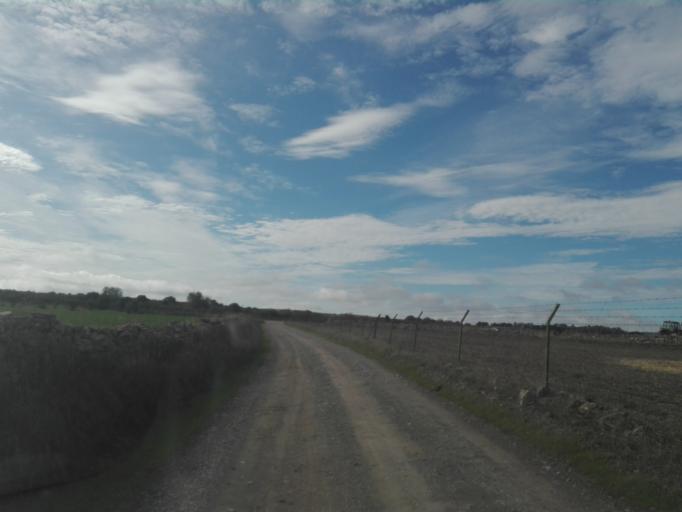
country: ES
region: Extremadura
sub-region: Provincia de Badajoz
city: Villagarcia de la Torre
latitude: 38.3027
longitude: -6.0861
